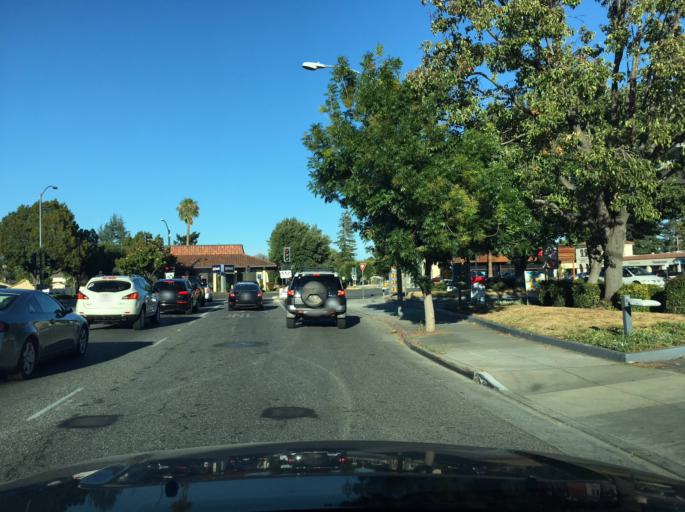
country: US
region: California
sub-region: Santa Clara County
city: Campbell
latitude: 37.2870
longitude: -121.9325
